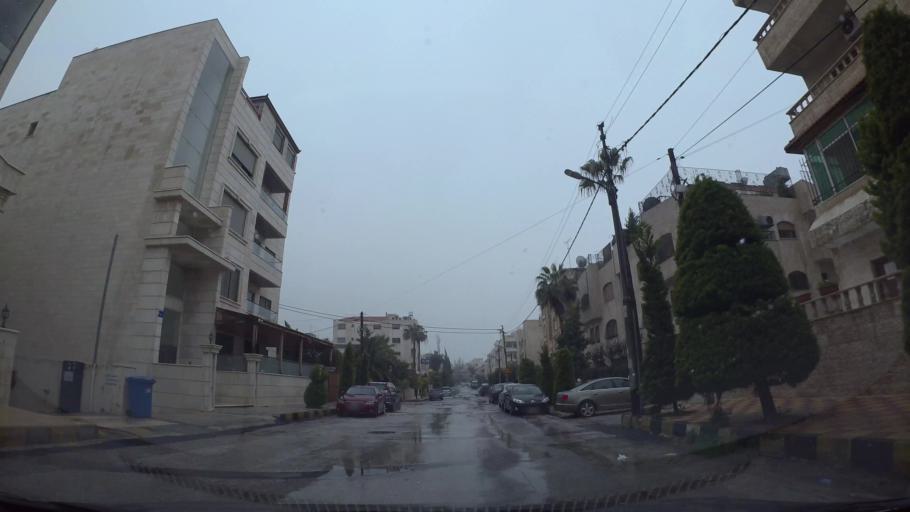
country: JO
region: Amman
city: Wadi as Sir
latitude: 31.9708
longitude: 35.8656
